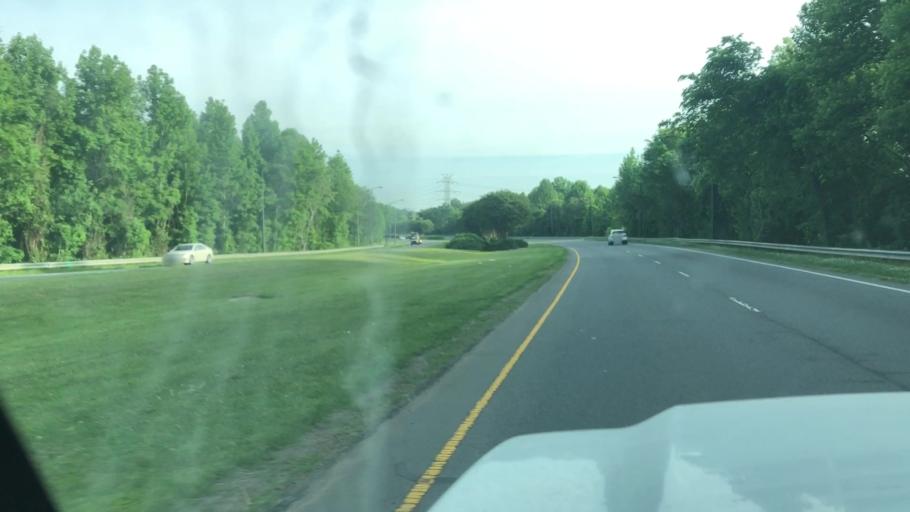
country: US
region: North Carolina
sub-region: Gaston County
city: Mount Holly
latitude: 35.3034
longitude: -80.9207
